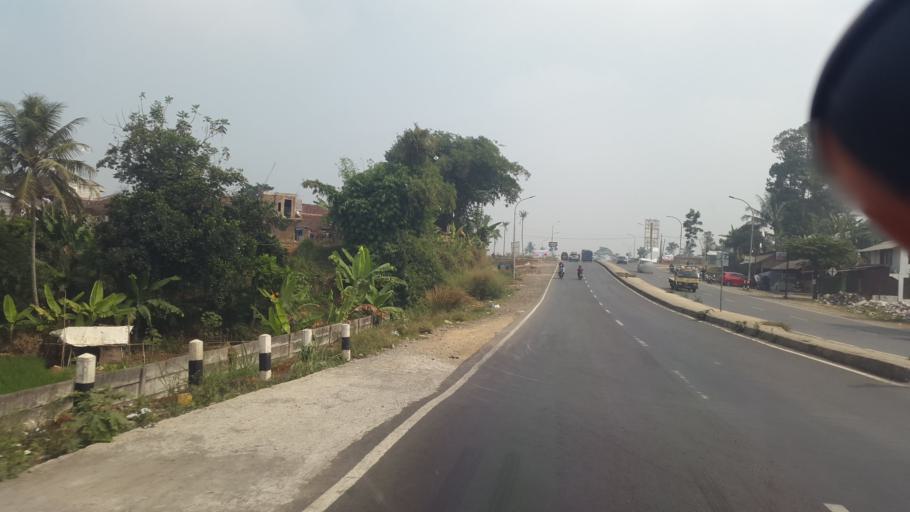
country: ID
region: West Java
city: Sukabumi
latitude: -6.9178
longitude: 106.8856
